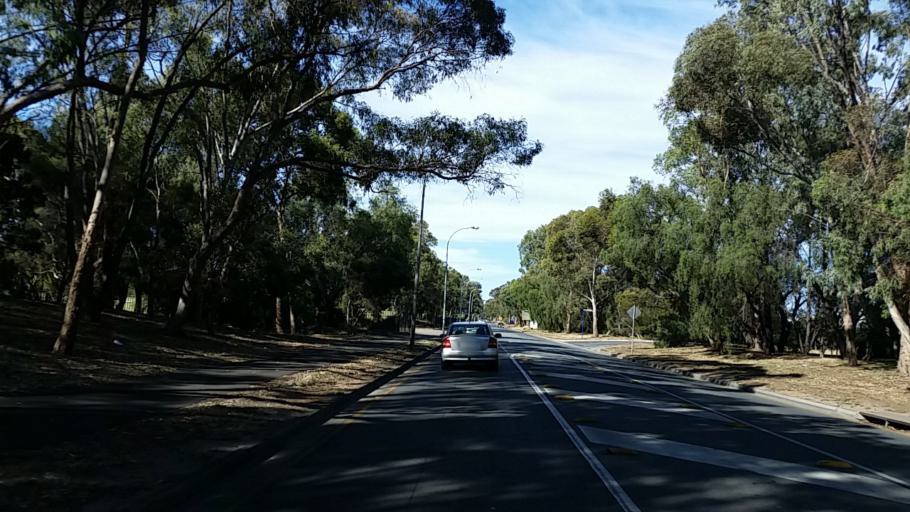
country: AU
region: South Australia
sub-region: Salisbury
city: Salisbury
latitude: -34.7840
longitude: 138.6378
